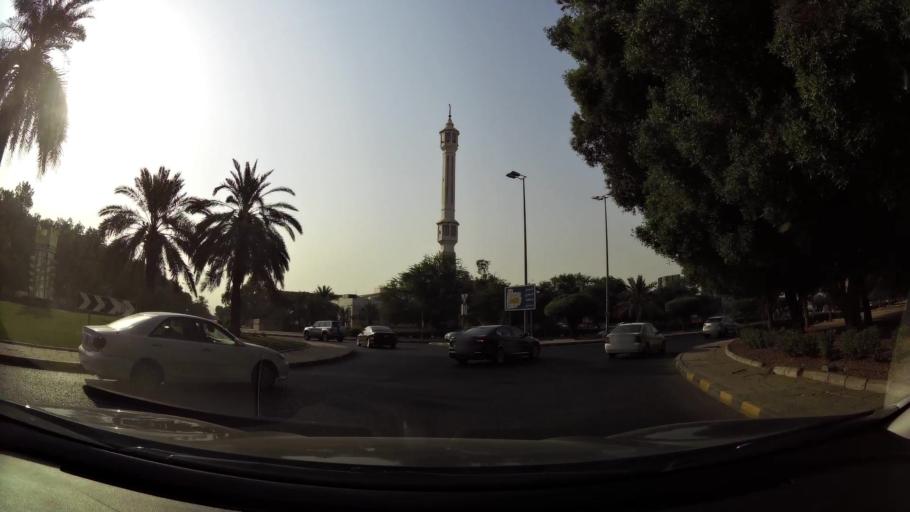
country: KW
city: Bayan
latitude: 29.3014
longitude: 48.0556
